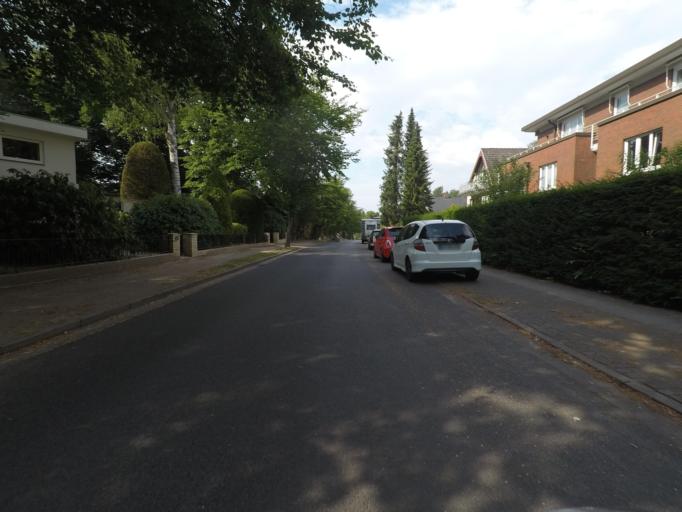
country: DE
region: Hamburg
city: Wellingsbuettel
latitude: 53.6365
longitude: 10.0649
